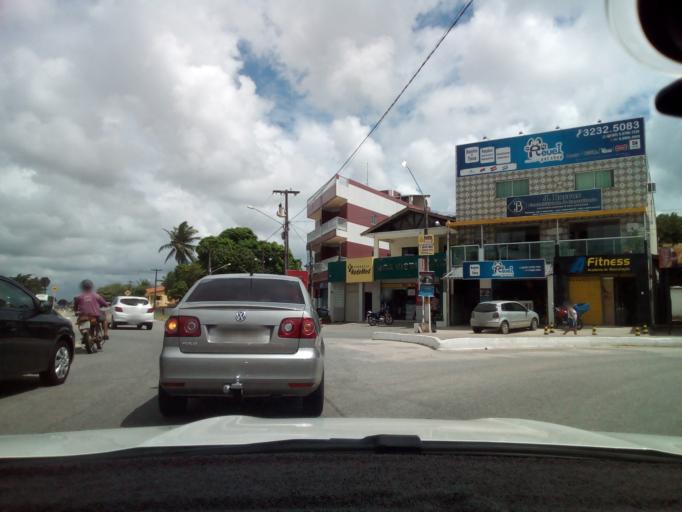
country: BR
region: Paraiba
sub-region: Bayeux
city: Bayeux
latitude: -7.1351
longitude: -34.9383
